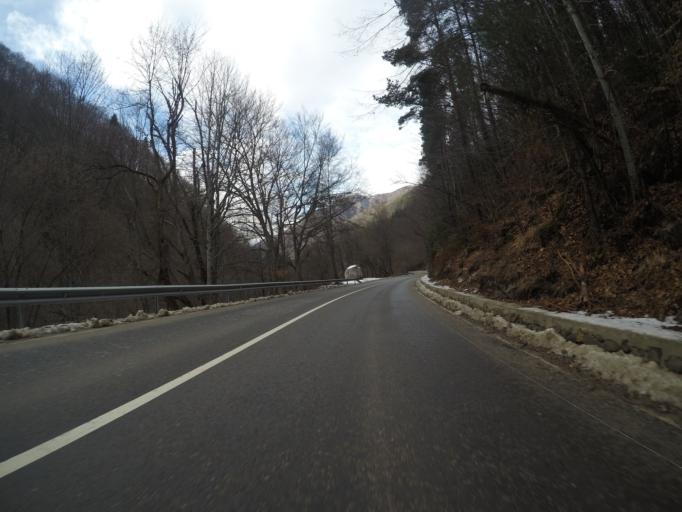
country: BG
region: Kyustendil
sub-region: Obshtina Rila
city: Rila
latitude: 42.1135
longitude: 23.3028
